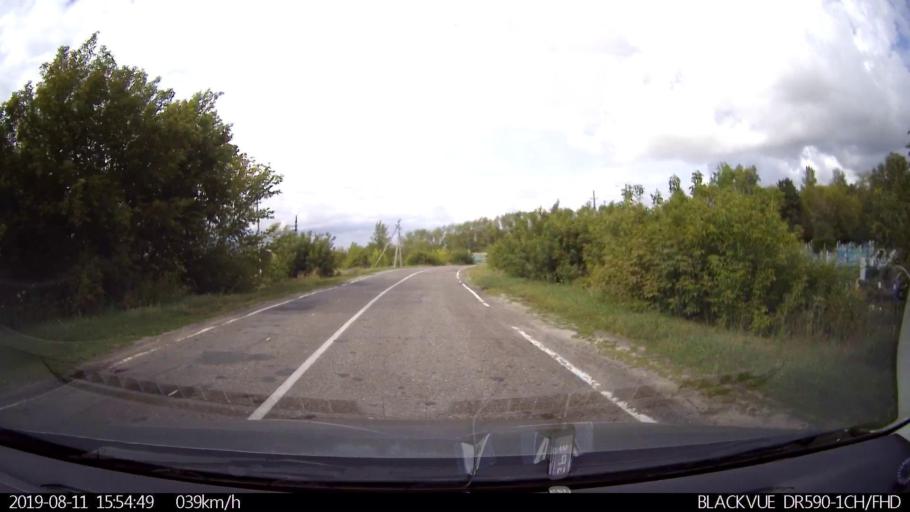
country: RU
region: Ulyanovsk
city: Ignatovka
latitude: 53.9431
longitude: 47.6560
